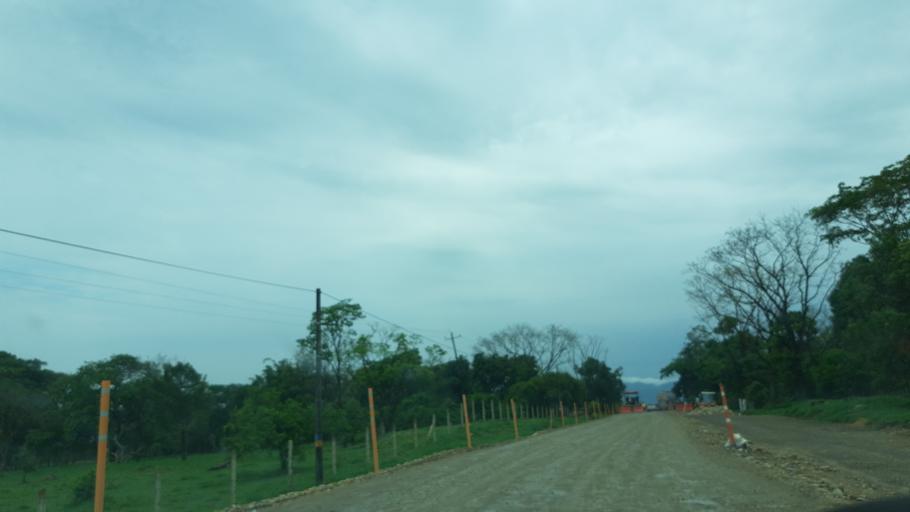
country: CO
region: Casanare
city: Monterrey
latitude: 4.8319
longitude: -72.9596
